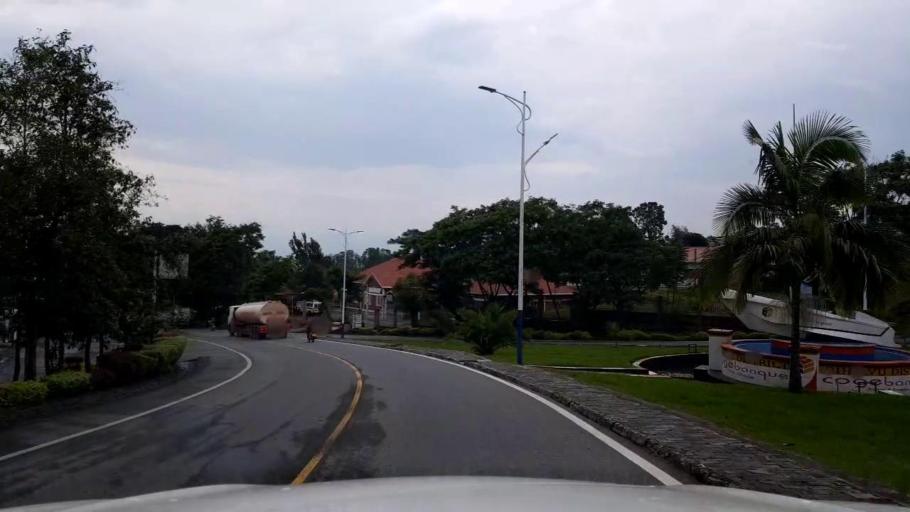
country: RW
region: Western Province
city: Gisenyi
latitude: -1.7028
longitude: 29.2632
